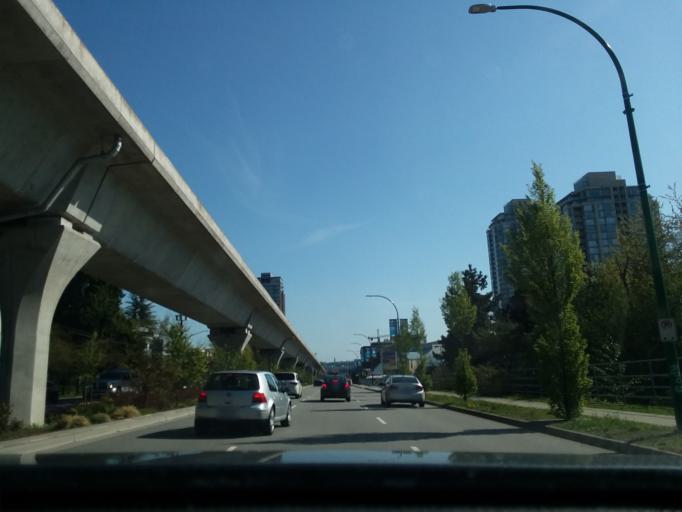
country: CA
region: British Columbia
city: Port Moody
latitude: 49.2551
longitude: -122.8931
